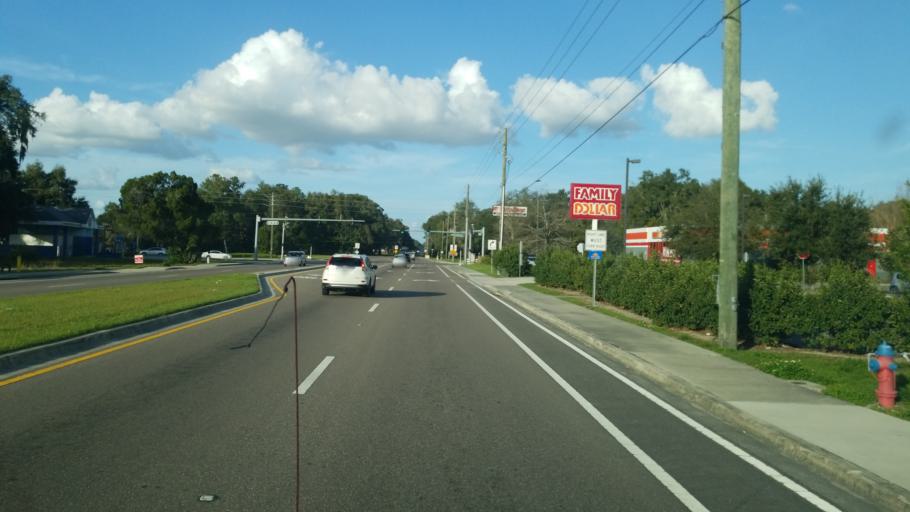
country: US
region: Florida
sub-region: Marion County
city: Ocala
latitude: 29.2219
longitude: -82.1241
